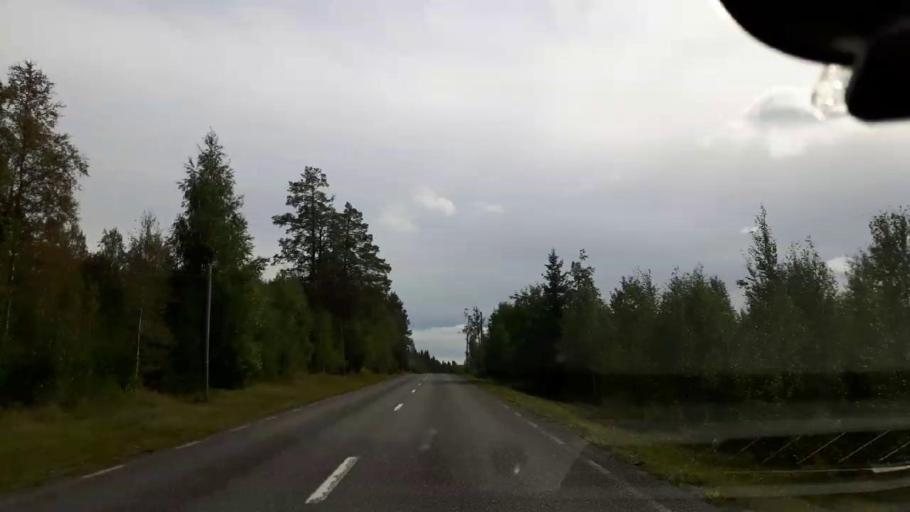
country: SE
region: Jaemtland
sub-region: Ragunda Kommun
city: Hammarstrand
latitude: 63.1349
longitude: 15.8752
